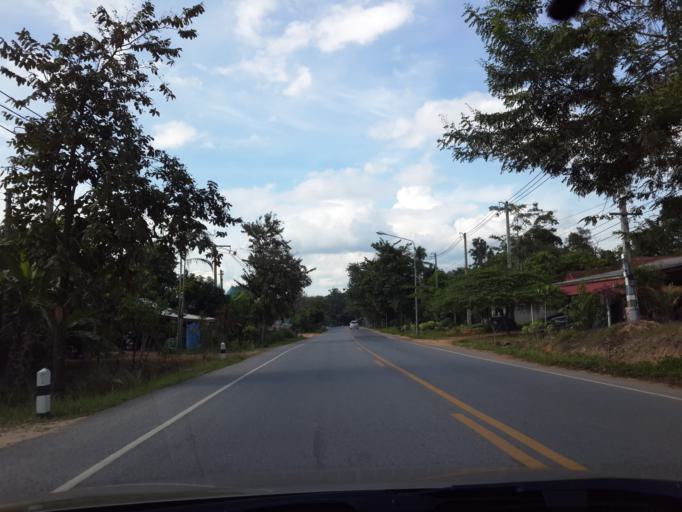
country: TH
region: Yala
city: Krong Pi Nang
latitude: 6.4687
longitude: 101.3269
